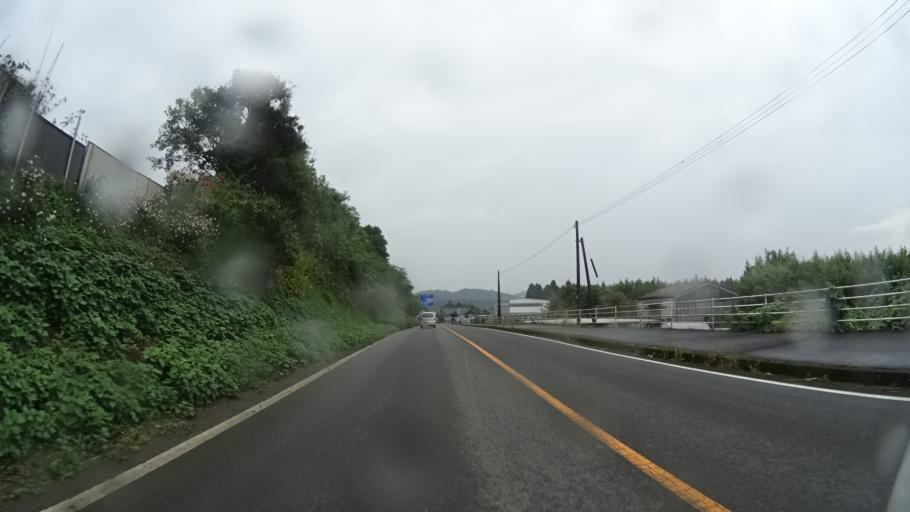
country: JP
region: Kagoshima
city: Kajiki
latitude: 31.8077
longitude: 130.6778
